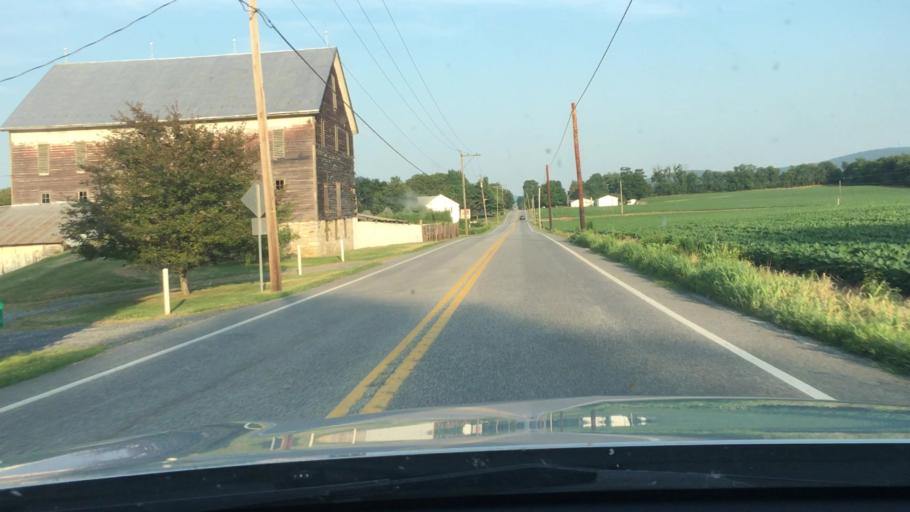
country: US
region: Pennsylvania
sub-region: Cumberland County
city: Boiling Springs
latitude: 40.1711
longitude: -77.1171
